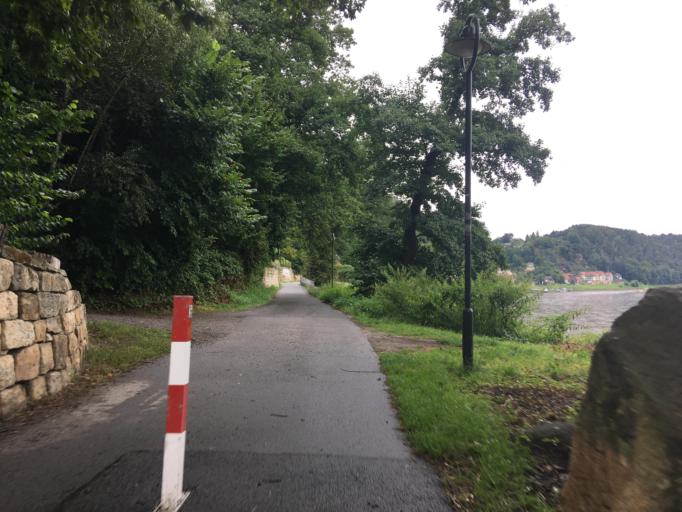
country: DE
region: Saxony
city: Stadt Wehlen
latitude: 50.9606
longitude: 14.0711
